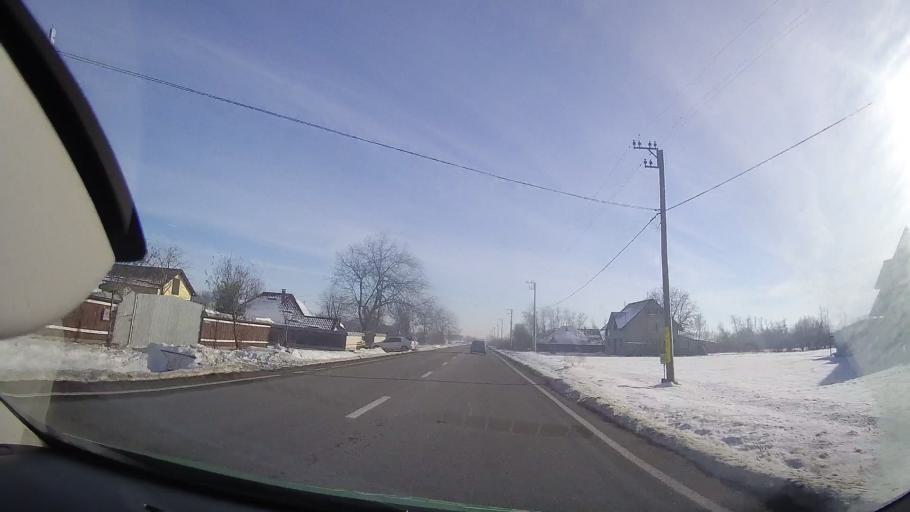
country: RO
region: Neamt
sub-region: Comuna Ghindaoani
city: Ghindaoani
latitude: 47.0835
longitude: 26.3390
